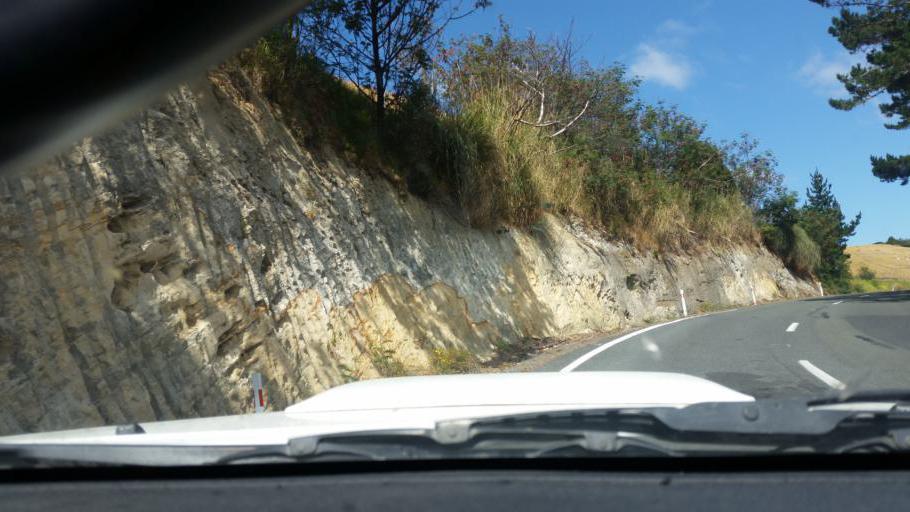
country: NZ
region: Northland
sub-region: Kaipara District
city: Dargaville
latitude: -35.8228
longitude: 173.6921
